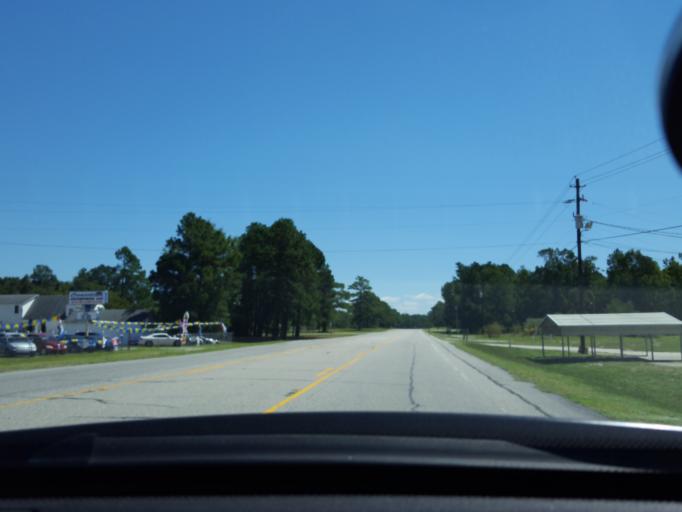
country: US
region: North Carolina
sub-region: Bladen County
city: Elizabethtown
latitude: 34.6484
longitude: -78.5680
